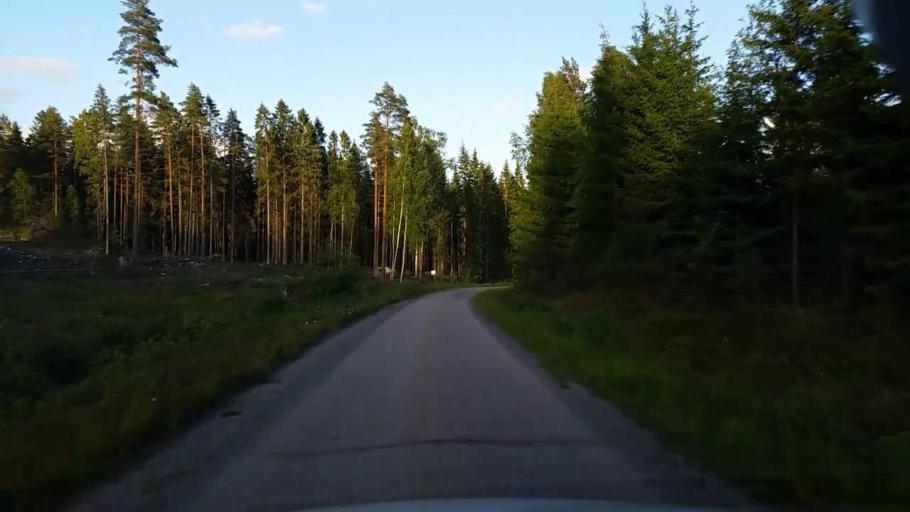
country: SE
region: Vaestmanland
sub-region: Kopings Kommun
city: Kolsva
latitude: 59.7072
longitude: 15.9331
